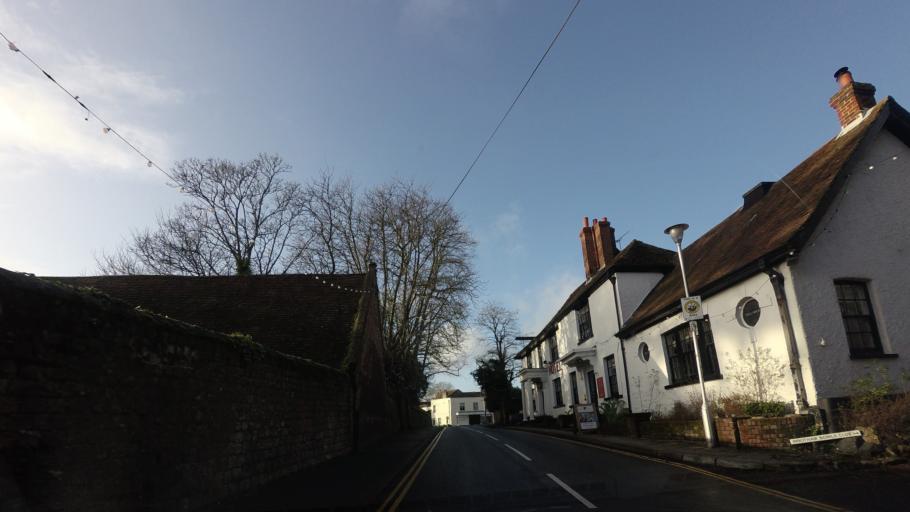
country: GB
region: England
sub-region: Kent
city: Borough Green
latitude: 51.3083
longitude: 0.3117
